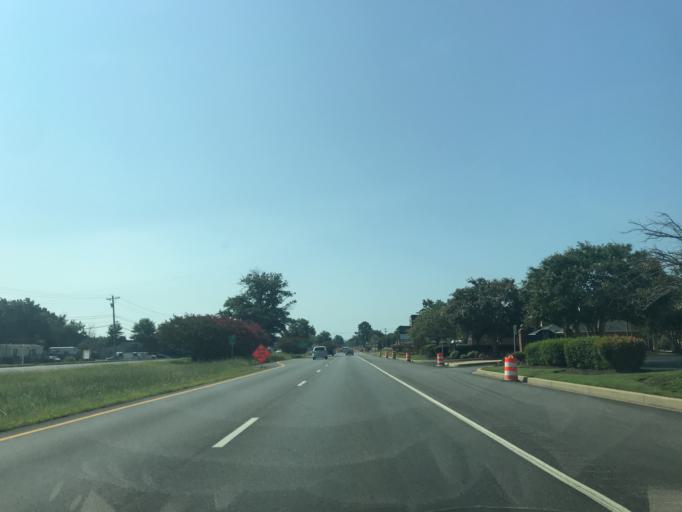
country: US
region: Maryland
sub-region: Saint Mary's County
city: Charlotte Hall
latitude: 38.4974
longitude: -76.7752
